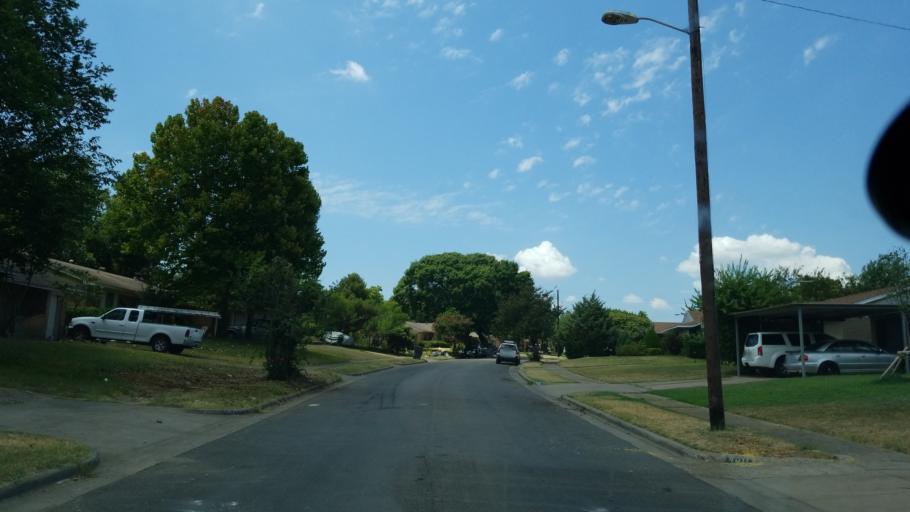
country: US
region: Texas
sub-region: Dallas County
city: Cockrell Hill
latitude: 32.7231
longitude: -96.8982
